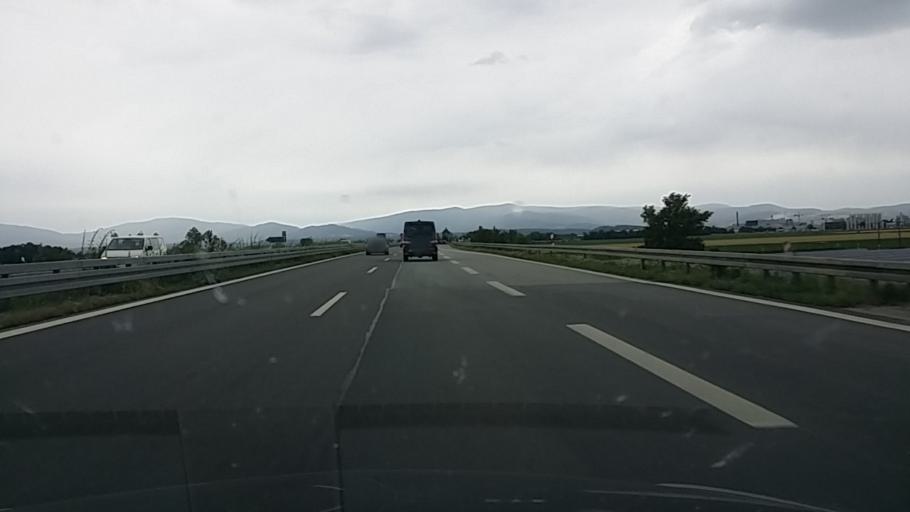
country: DE
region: Bavaria
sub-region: Lower Bavaria
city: Otzing
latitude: 48.7917
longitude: 12.8353
